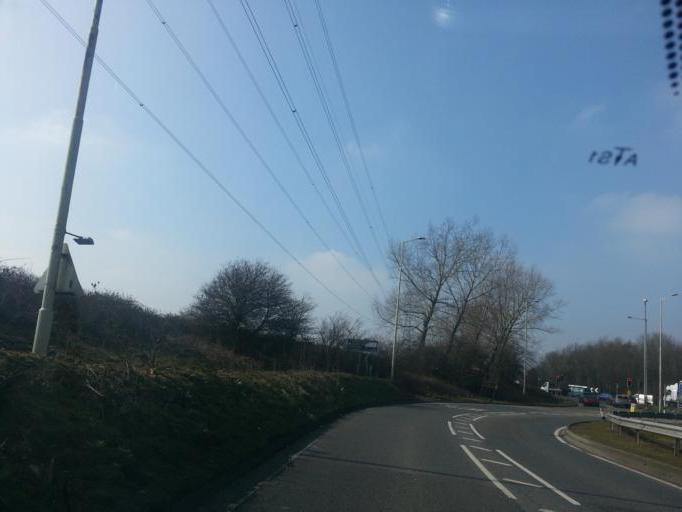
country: GB
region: England
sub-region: Greater London
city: High Barnet
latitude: 51.6843
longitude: -0.2275
